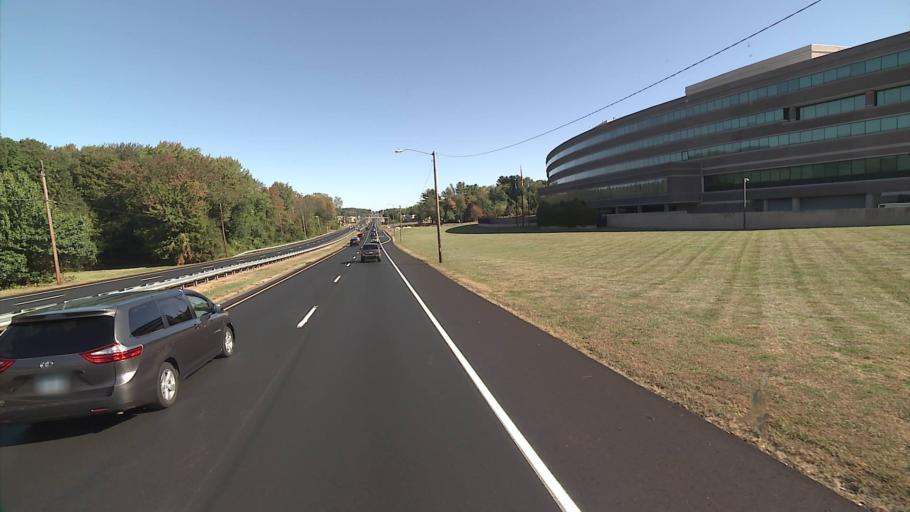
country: US
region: Connecticut
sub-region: Hartford County
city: Newington
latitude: 41.6728
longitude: -72.7160
